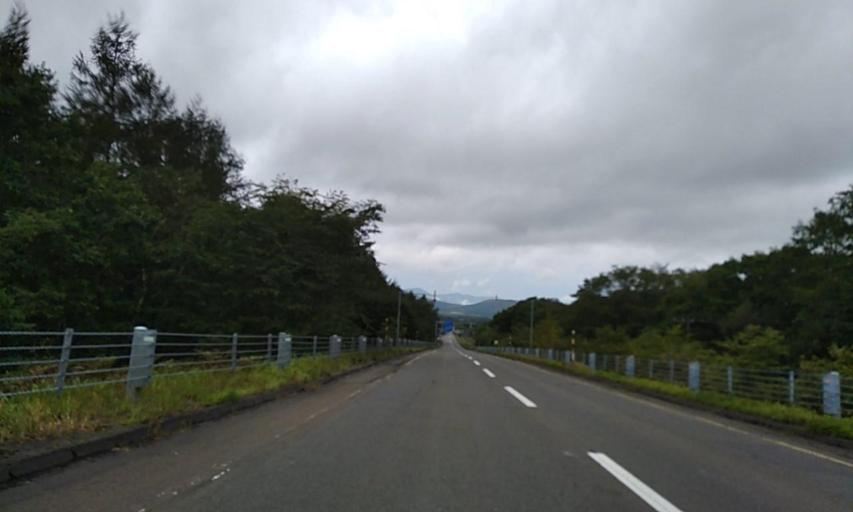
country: JP
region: Hokkaido
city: Bihoro
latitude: 43.5145
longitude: 144.4364
